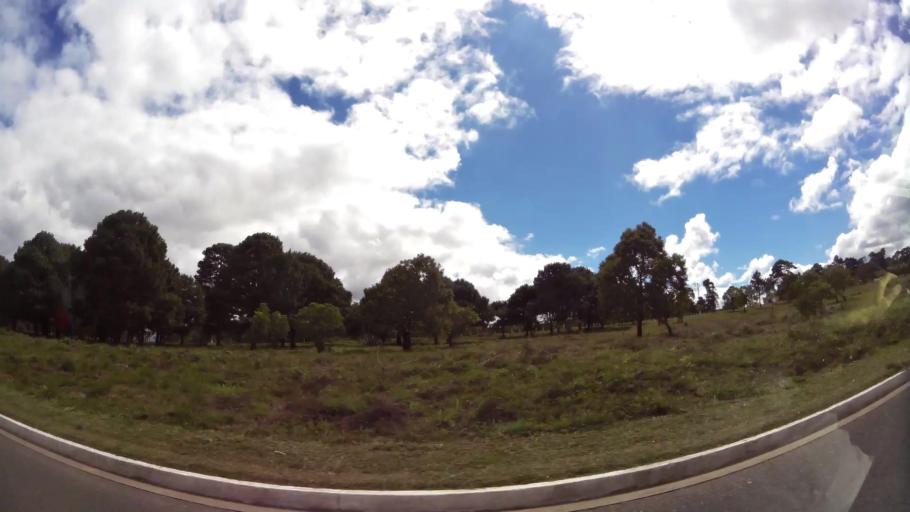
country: GT
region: Guatemala
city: Guatemala City
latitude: 14.6550
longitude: -90.5443
